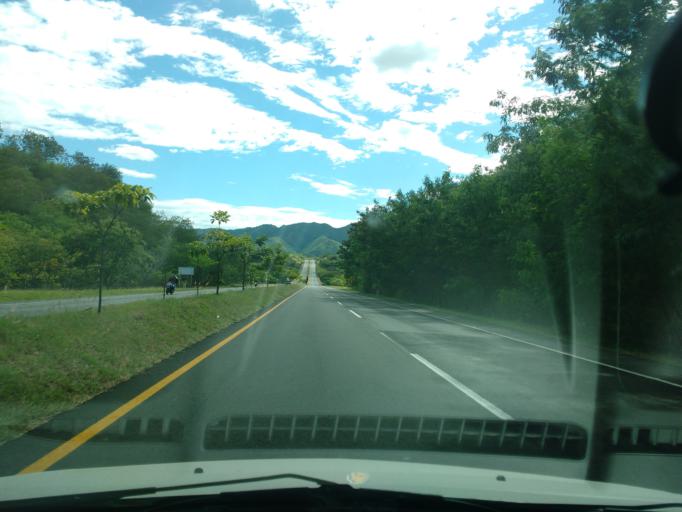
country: CO
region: Tolima
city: Espinal
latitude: 4.2324
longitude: -74.9150
